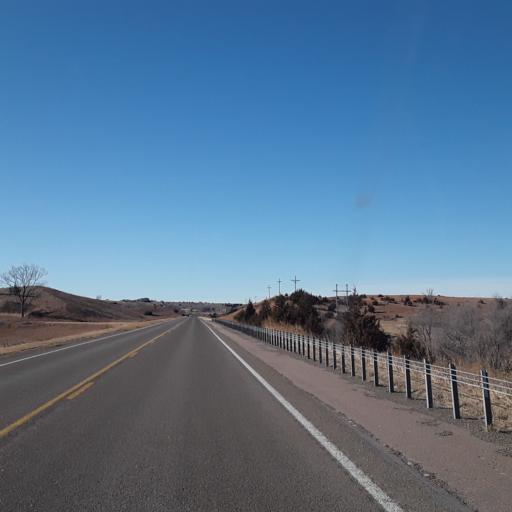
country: US
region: Nebraska
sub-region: Frontier County
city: Stockville
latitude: 40.6303
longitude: -100.5555
